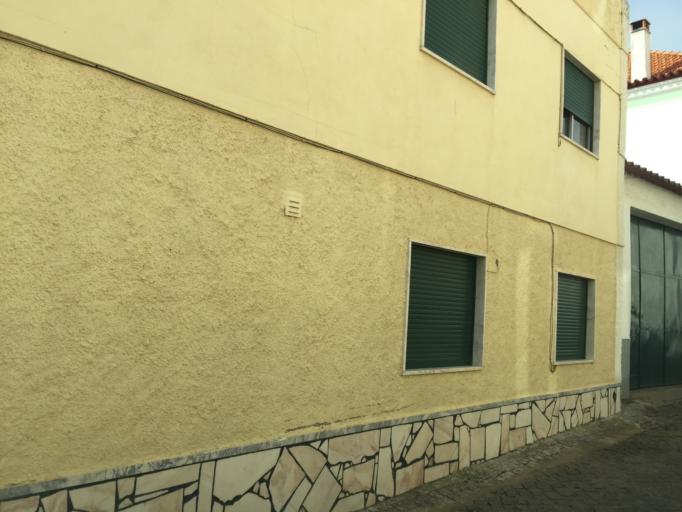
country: PT
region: Portalegre
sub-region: Fronteira
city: Fronteira
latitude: 39.0561
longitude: -7.6494
